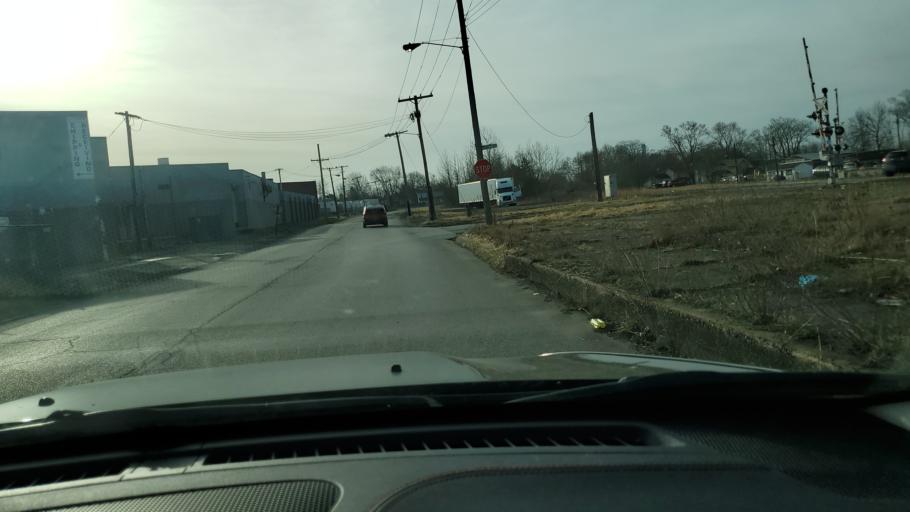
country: US
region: Ohio
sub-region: Trumbull County
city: Niles
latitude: 41.1813
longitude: -80.7576
